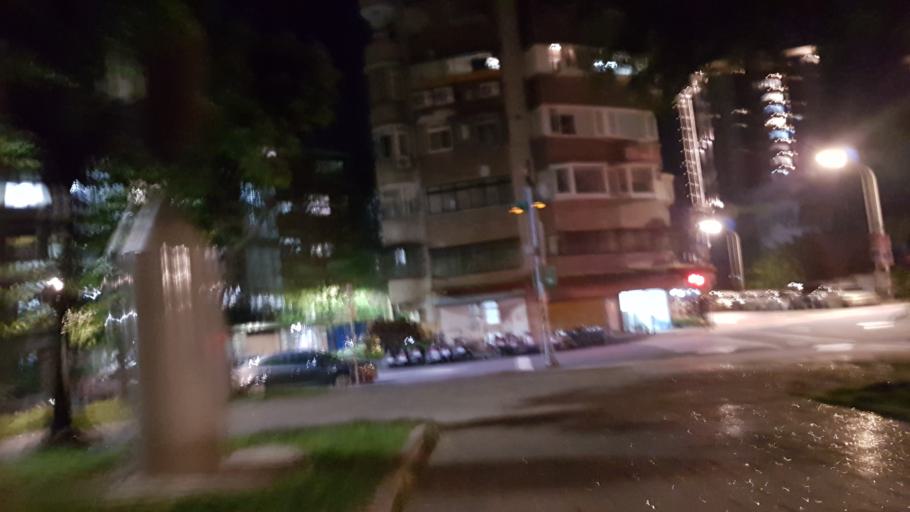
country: TW
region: Taipei
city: Taipei
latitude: 24.9984
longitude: 121.5367
